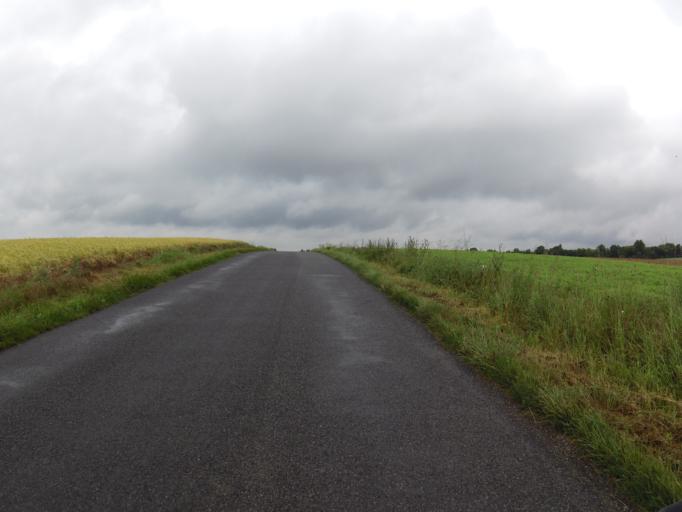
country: FR
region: Poitou-Charentes
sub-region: Departement de la Charente
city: Balzac
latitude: 45.7133
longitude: 0.1314
